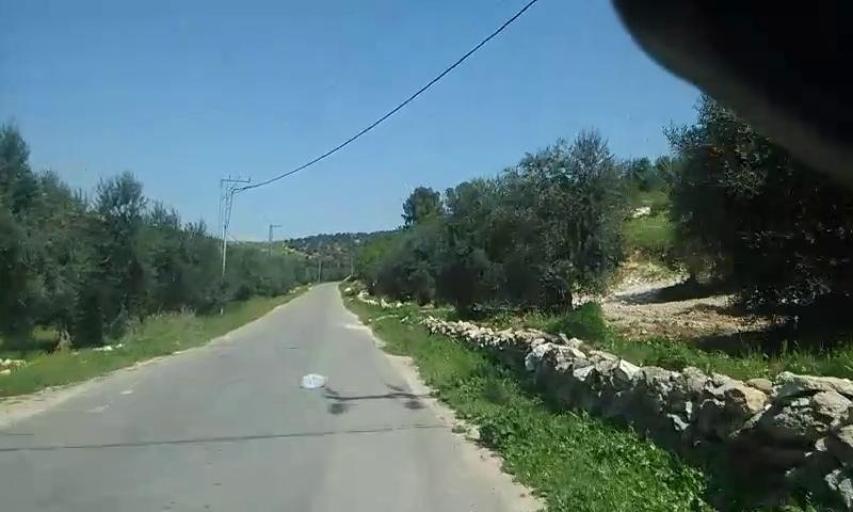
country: PS
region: West Bank
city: Al Majd
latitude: 31.4908
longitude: 34.9503
